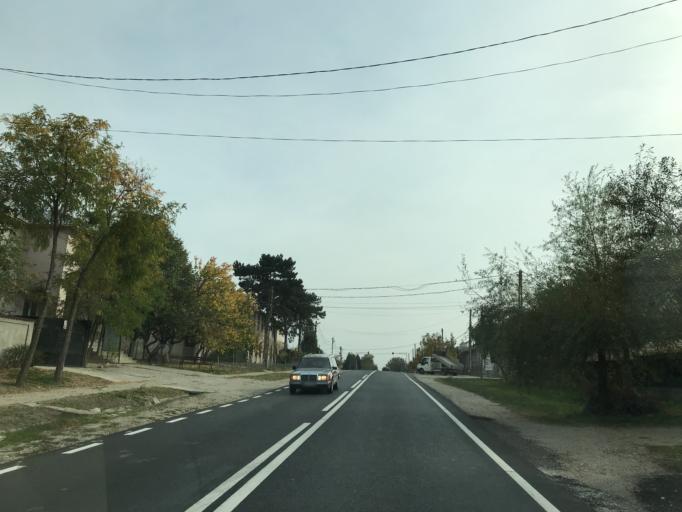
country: RO
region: Olt
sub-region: Comuna Piatra Olt
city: Piatra
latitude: 44.3619
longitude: 24.2937
